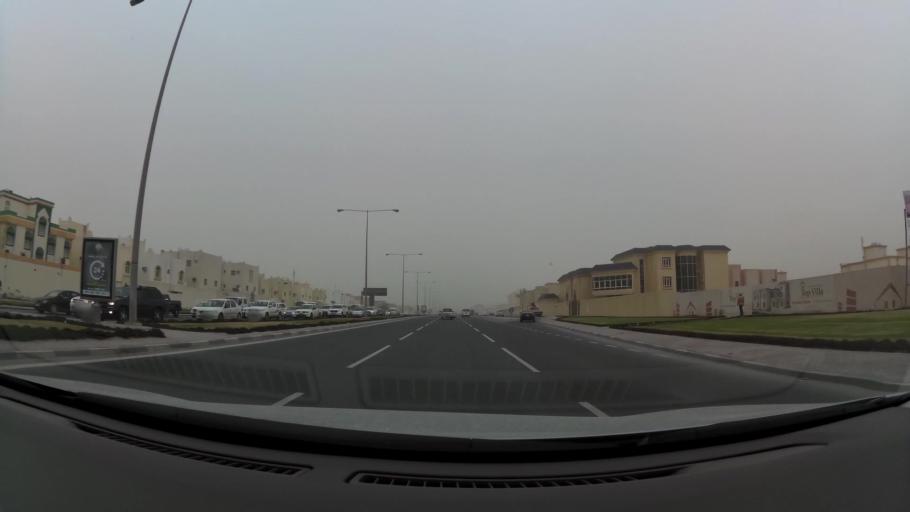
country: QA
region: Baladiyat ad Dawhah
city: Doha
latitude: 25.2516
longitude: 51.4885
